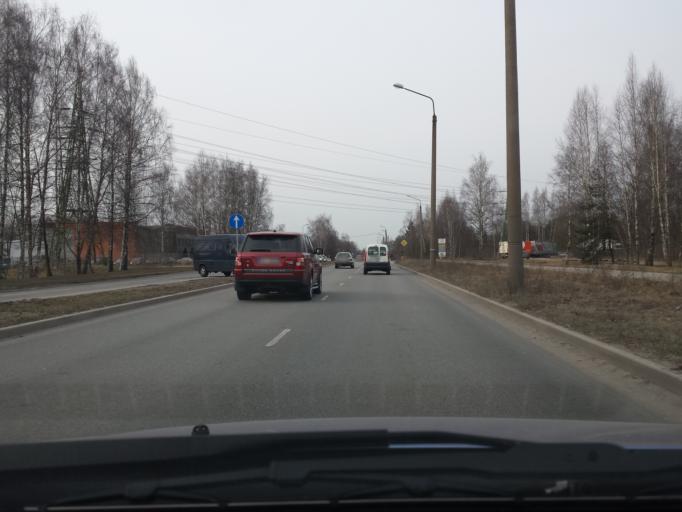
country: LV
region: Kekava
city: Balozi
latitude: 56.9081
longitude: 24.1276
